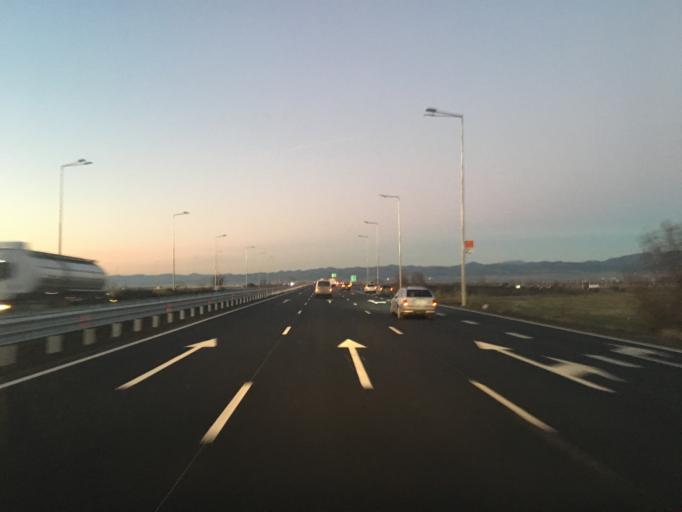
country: BG
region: Sofia-Capital
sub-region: Stolichna Obshtina
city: Sofia
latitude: 42.7033
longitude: 23.4506
